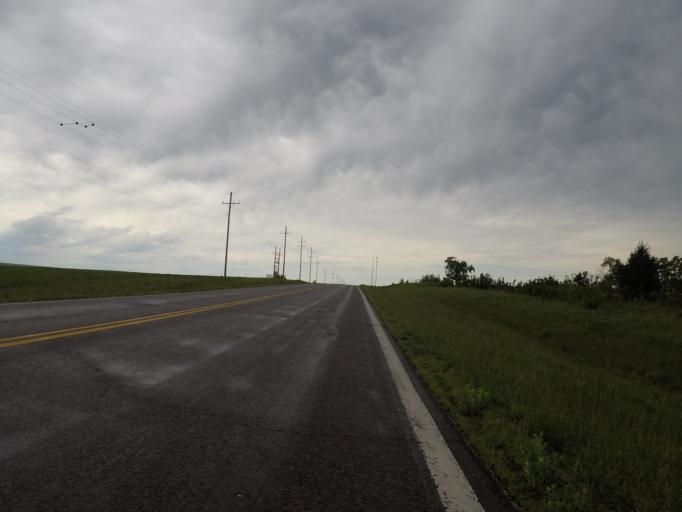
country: US
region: Kansas
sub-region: Wabaunsee County
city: Alma
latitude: 38.8665
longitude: -96.1252
